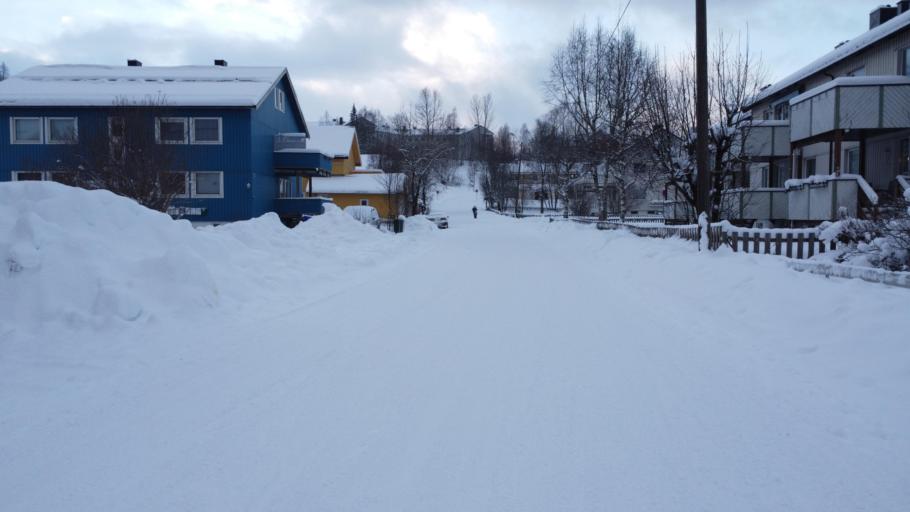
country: NO
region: Nordland
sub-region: Rana
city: Mo i Rana
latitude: 66.3188
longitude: 14.1652
